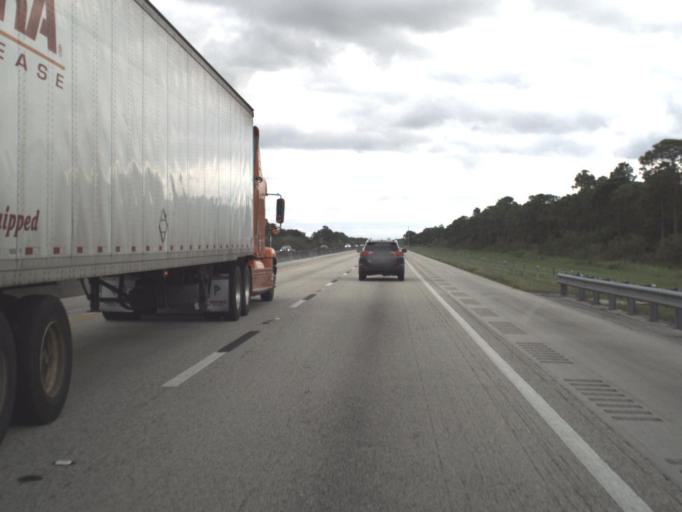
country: US
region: Florida
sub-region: Martin County
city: Port Salerno
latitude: 27.0774
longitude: -80.2494
